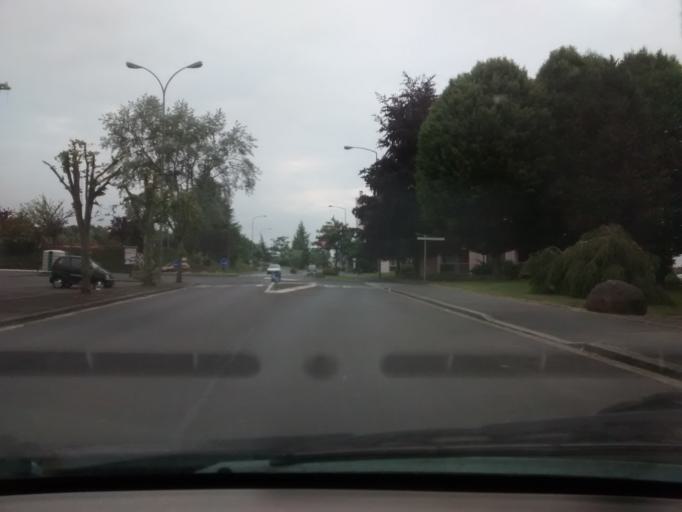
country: FR
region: Lower Normandy
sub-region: Departement de la Manche
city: Saint-Lo
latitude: 49.1107
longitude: -1.0717
